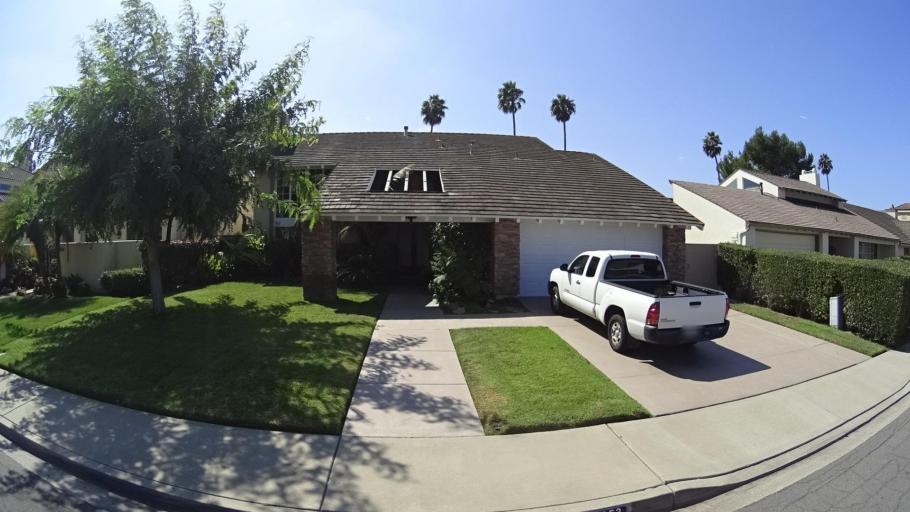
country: US
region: California
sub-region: San Diego County
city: Fairbanks Ranch
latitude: 32.9874
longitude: -117.2125
